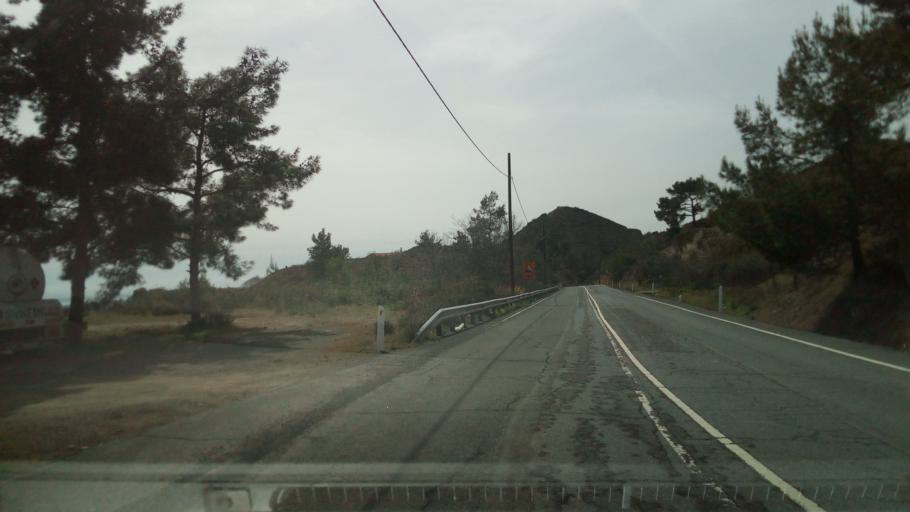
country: CY
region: Limassol
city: Pelendri
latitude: 34.8807
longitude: 32.9465
